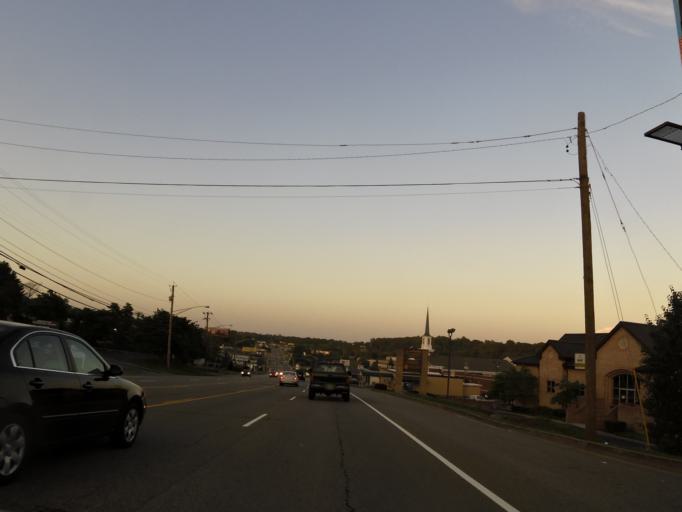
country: US
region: Tennessee
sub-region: Knox County
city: Knoxville
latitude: 35.9318
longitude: -84.0077
